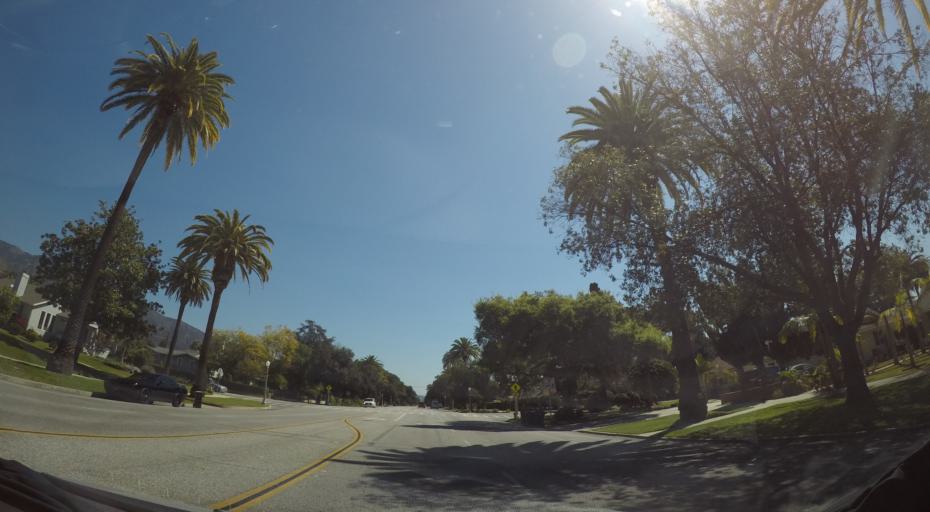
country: US
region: California
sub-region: Los Angeles County
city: East Pasadena
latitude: 34.1578
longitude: -118.1183
